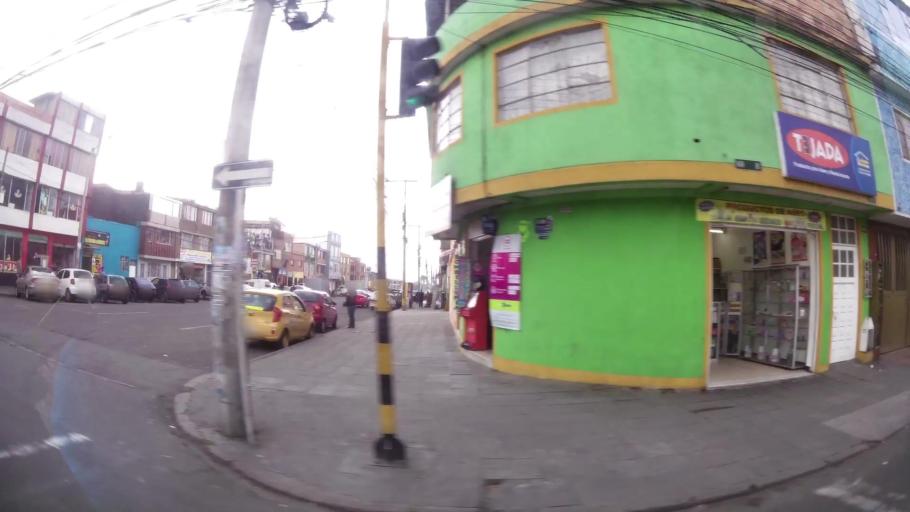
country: CO
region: Bogota D.C.
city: Bogota
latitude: 4.5719
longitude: -74.0954
